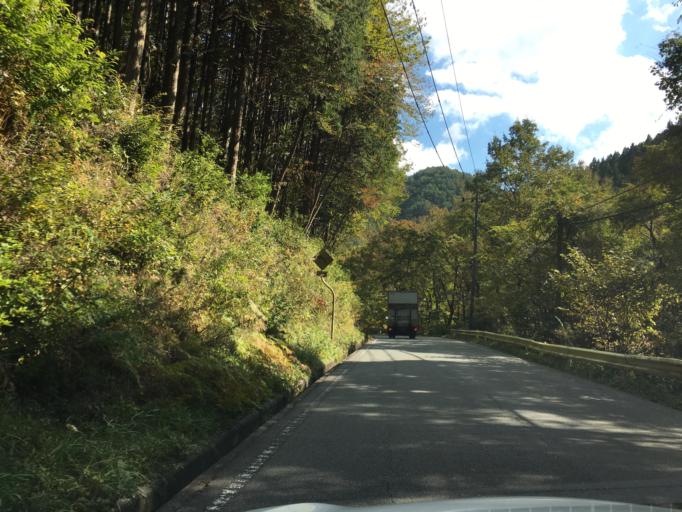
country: JP
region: Fukushima
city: Namie
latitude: 37.3462
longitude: 140.8864
